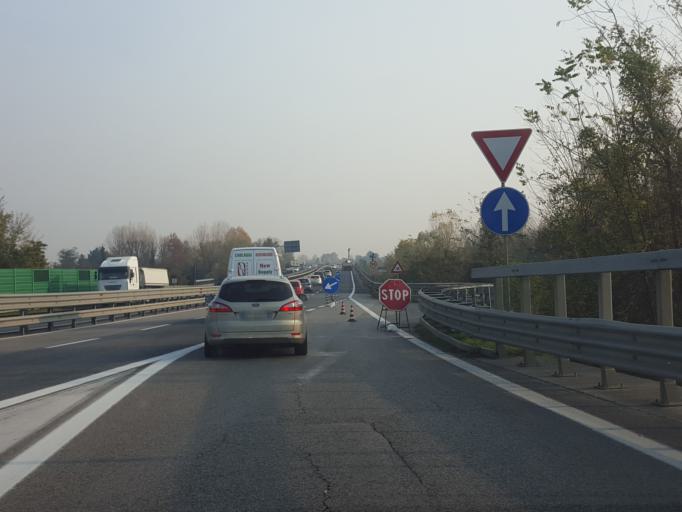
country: IT
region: Veneto
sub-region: Provincia di Treviso
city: Treviso
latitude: 45.6548
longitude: 12.2128
